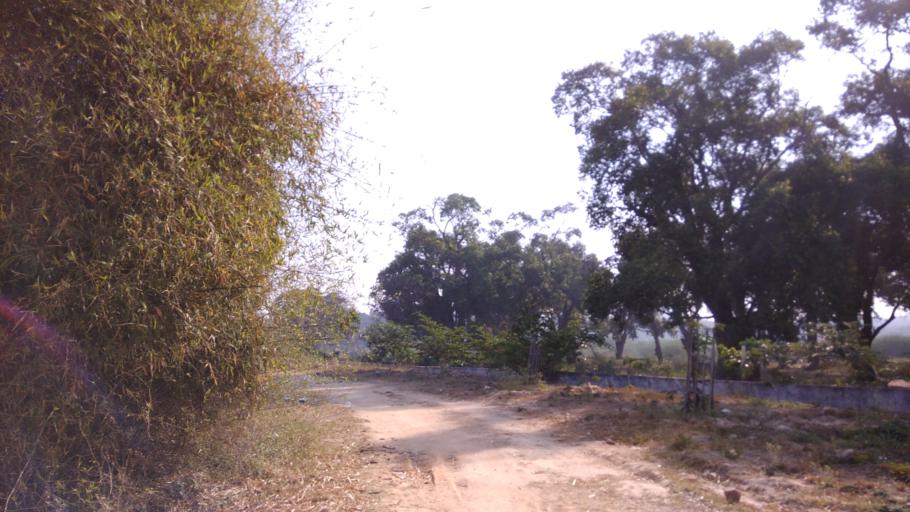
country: IN
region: Karnataka
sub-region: Bangalore Rural
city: Hoskote
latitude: 12.9728
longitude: 77.7349
